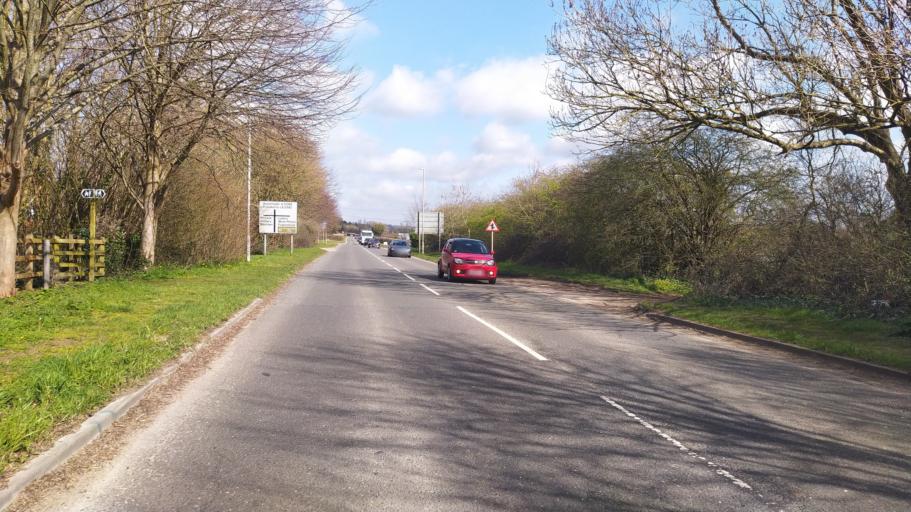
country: GB
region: England
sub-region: Dorset
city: Bridport
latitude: 50.7482
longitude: -2.7426
